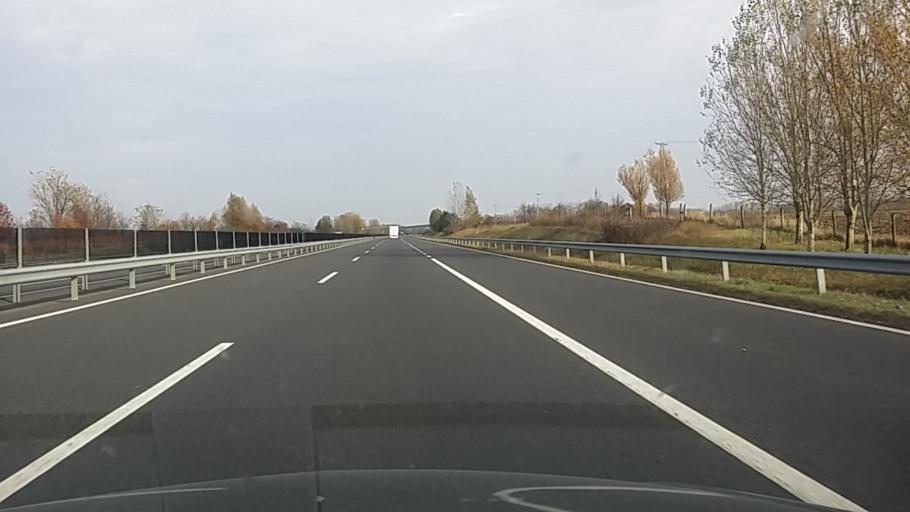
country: HU
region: Szabolcs-Szatmar-Bereg
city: Kalmanhaza
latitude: 47.9016
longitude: 21.5626
